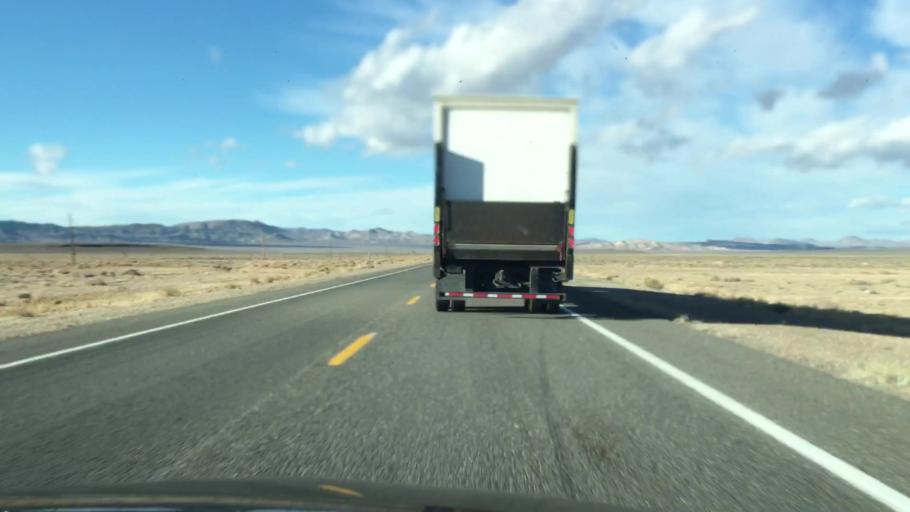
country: US
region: Nevada
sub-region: Esmeralda County
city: Goldfield
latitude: 37.4331
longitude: -117.1616
